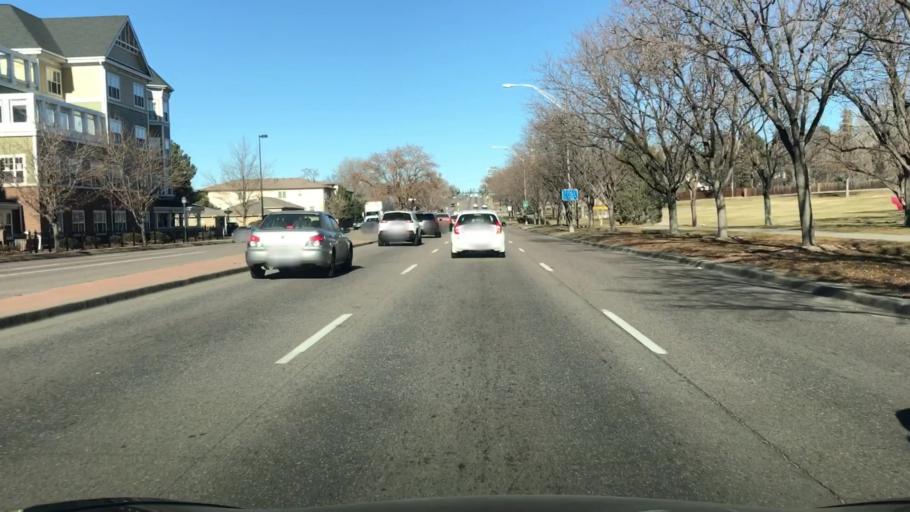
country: US
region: Colorado
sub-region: Arapahoe County
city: Glendale
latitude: 39.7122
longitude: -104.9406
